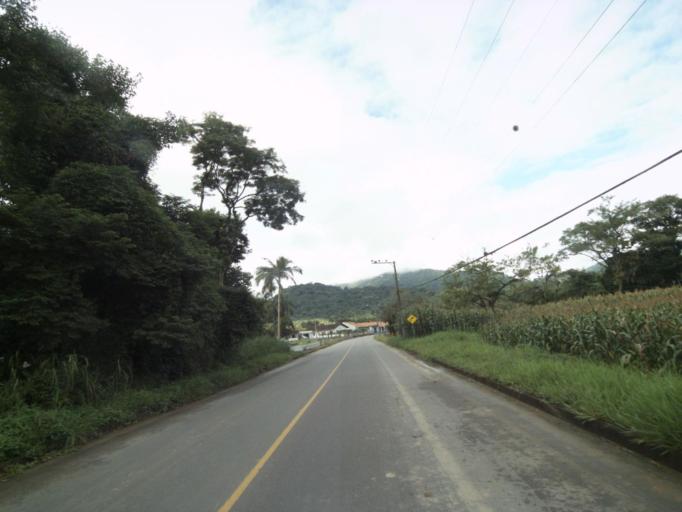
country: BR
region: Santa Catarina
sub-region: Pomerode
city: Pomerode
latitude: -26.7655
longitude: -49.1765
